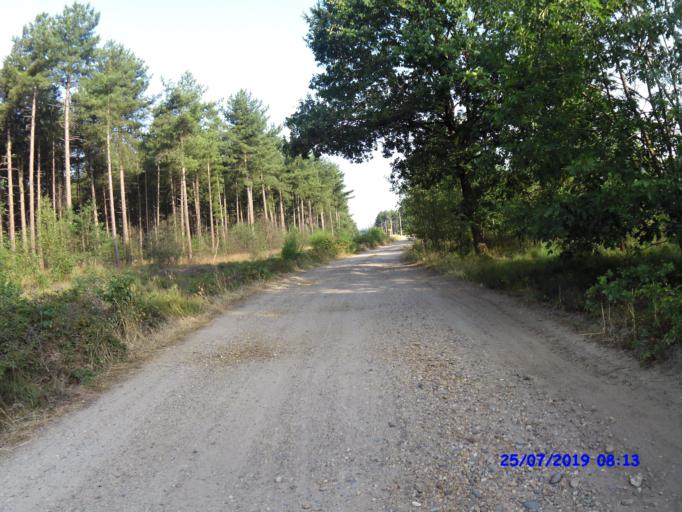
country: BE
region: Flanders
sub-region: Provincie Limburg
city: Lommel
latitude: 51.1777
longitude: 5.3062
